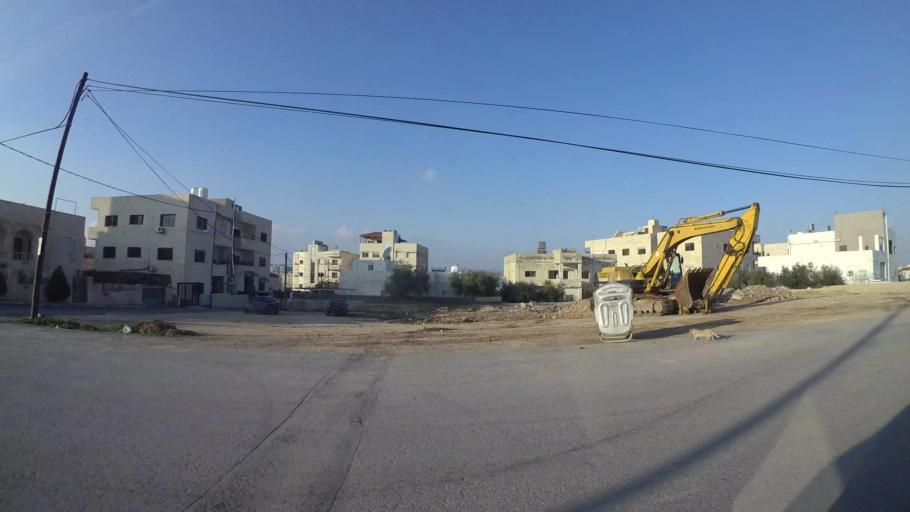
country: JO
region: Amman
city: Amman
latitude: 31.9842
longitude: 35.9675
